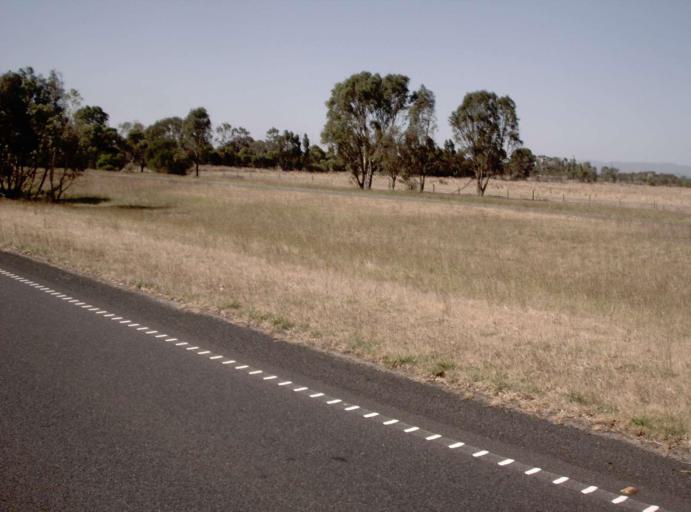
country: AU
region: Victoria
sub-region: Kingston
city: Chelsea Heights
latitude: -38.0343
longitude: 145.1380
